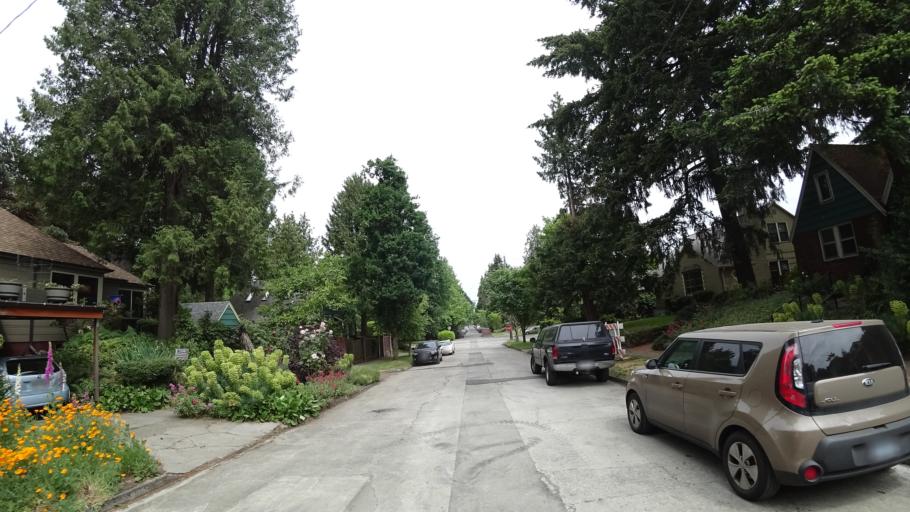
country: US
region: Oregon
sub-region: Multnomah County
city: Portland
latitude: 45.5658
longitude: -122.6361
